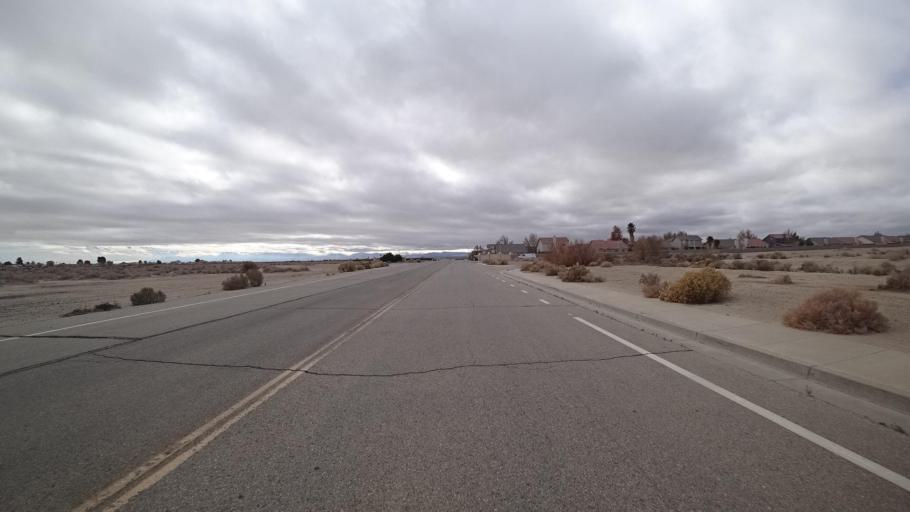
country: US
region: California
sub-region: Kern County
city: Rosamond
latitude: 34.8507
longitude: -118.1760
